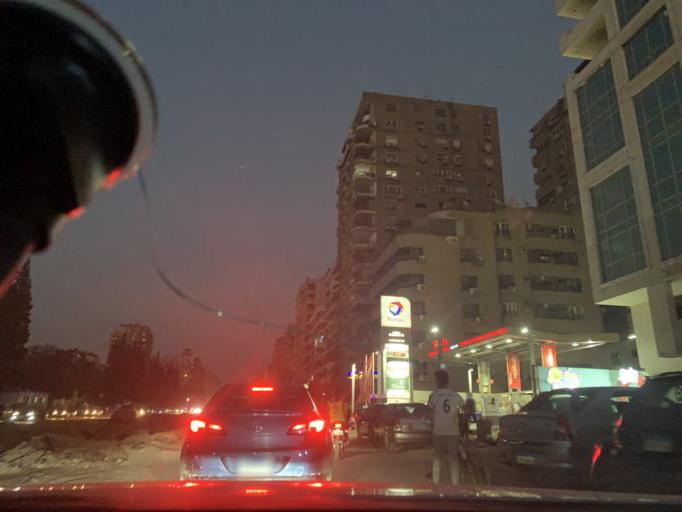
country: EG
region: Muhafazat al Qahirah
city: Cairo
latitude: 30.0604
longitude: 31.3464
